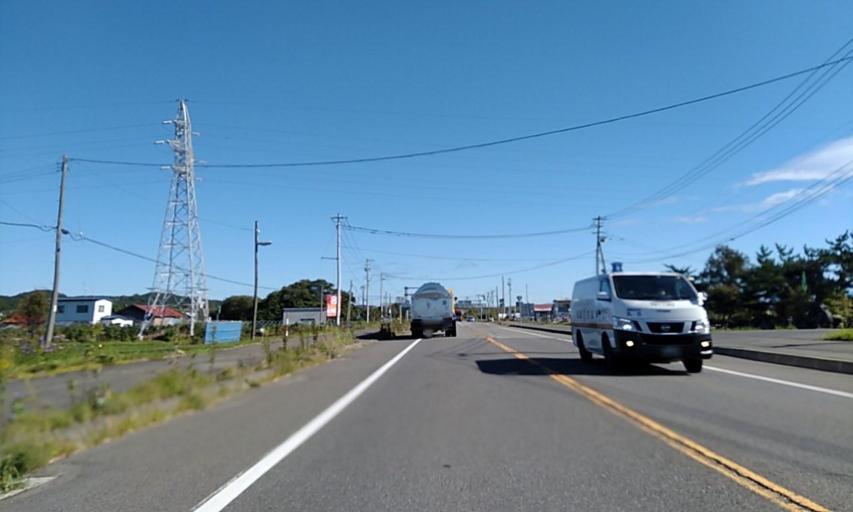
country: JP
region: Hokkaido
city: Shizunai-furukawacho
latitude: 42.5239
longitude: 142.0392
